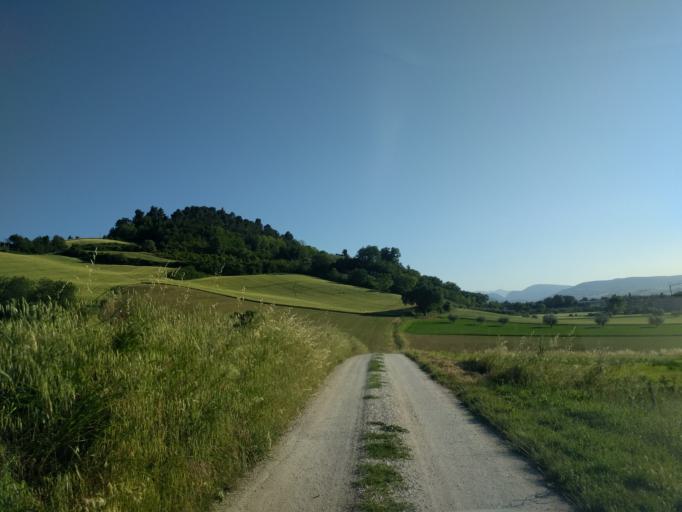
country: IT
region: The Marches
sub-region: Provincia di Pesaro e Urbino
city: Montemaggiore al Metauro
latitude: 43.7428
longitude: 12.9509
